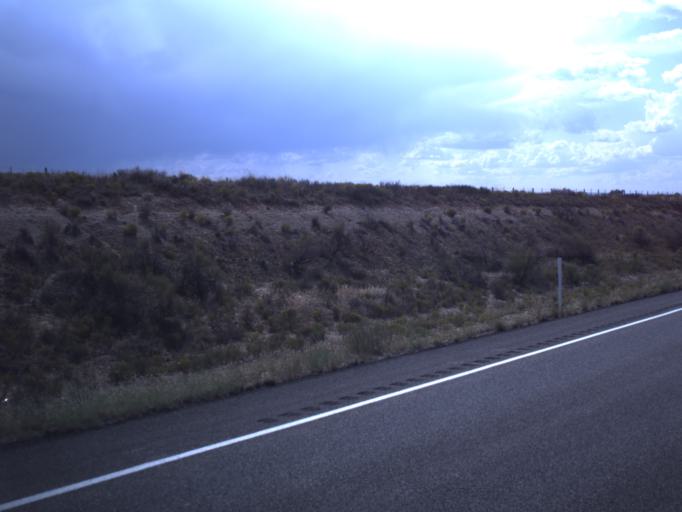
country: US
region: Arizona
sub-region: Coconino County
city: Page
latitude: 37.0989
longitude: -111.7886
